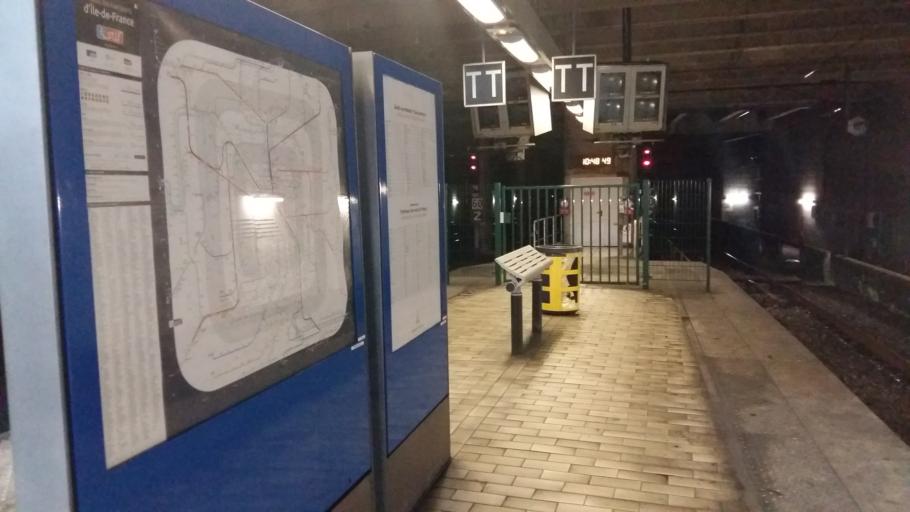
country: FR
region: Ile-de-France
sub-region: Departement du Val-d'Oise
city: Roissy-en-France
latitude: 49.0098
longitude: 2.5599
